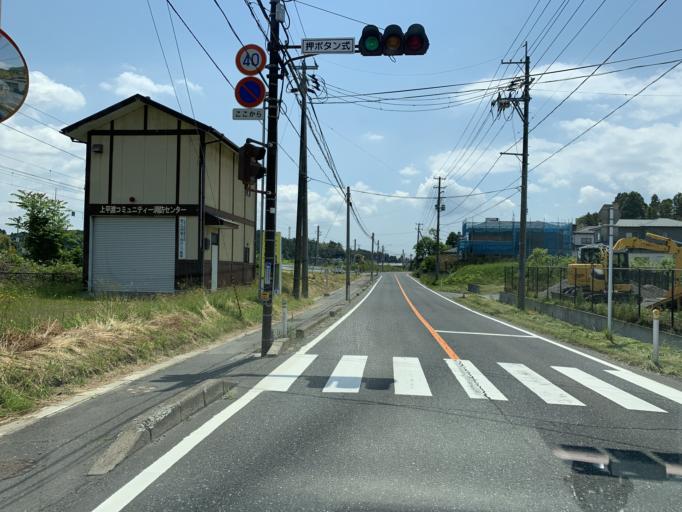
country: JP
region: Miyagi
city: Wakuya
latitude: 38.4858
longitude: 141.0956
